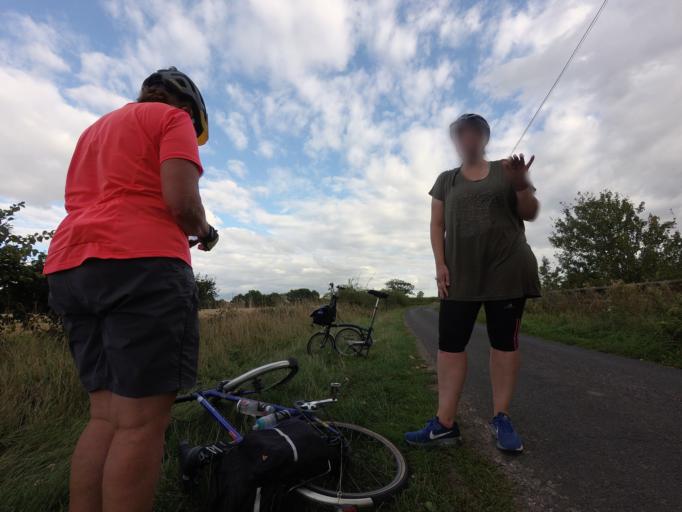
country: GB
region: England
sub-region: Kent
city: Staplehurst
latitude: 51.2069
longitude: 0.5386
